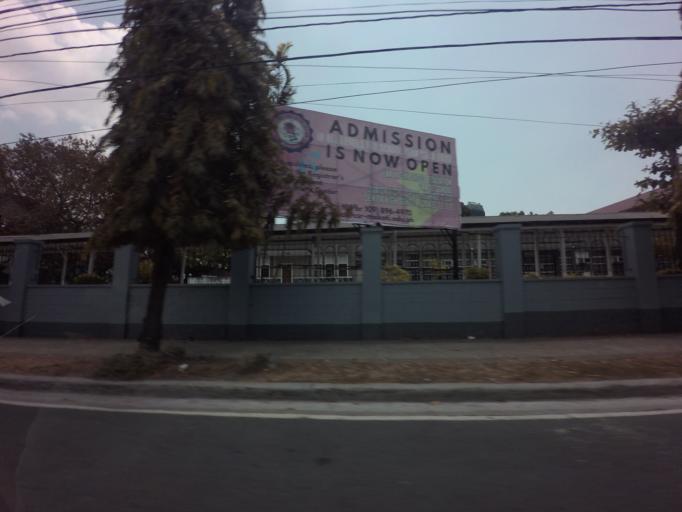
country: PH
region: Metro Manila
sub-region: Makati City
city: Makati City
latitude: 14.5621
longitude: 121.0395
